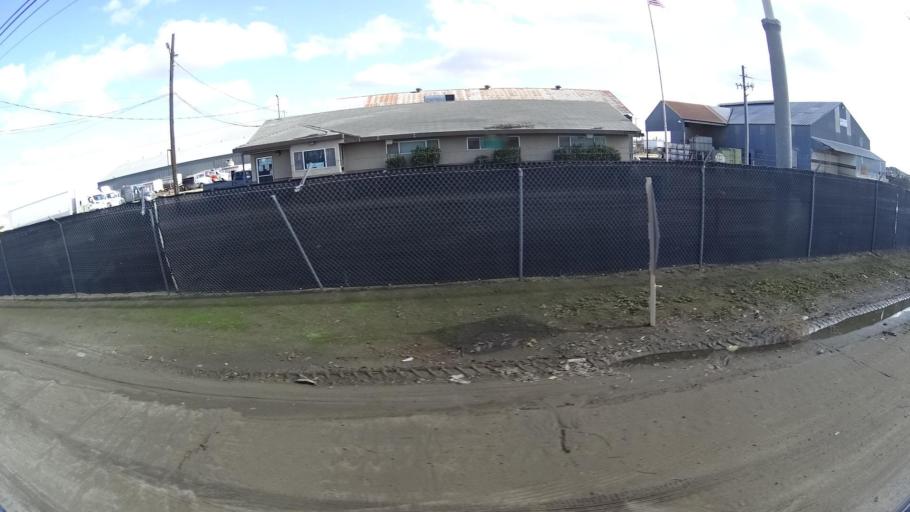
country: US
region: California
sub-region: Kern County
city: McFarland
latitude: 35.6895
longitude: -119.2408
